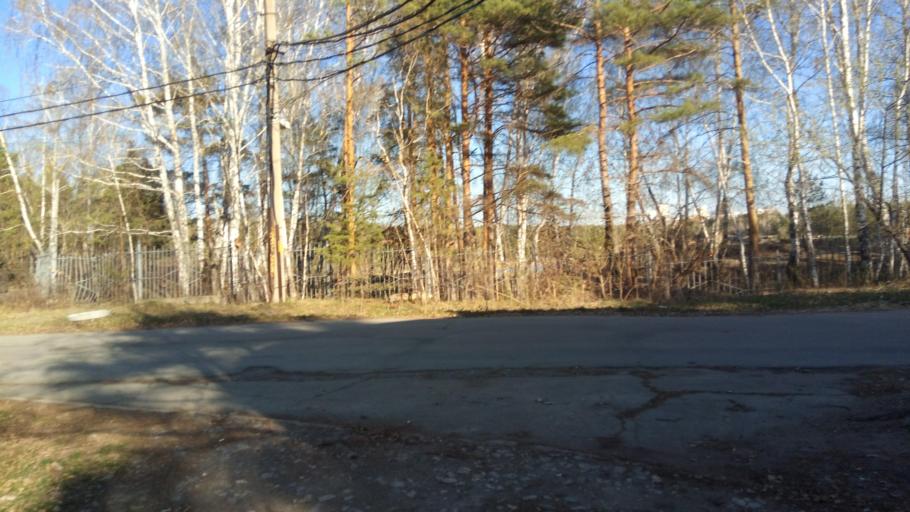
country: RU
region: Chelyabinsk
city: Novosineglazovskiy
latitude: 55.1258
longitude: 61.3301
